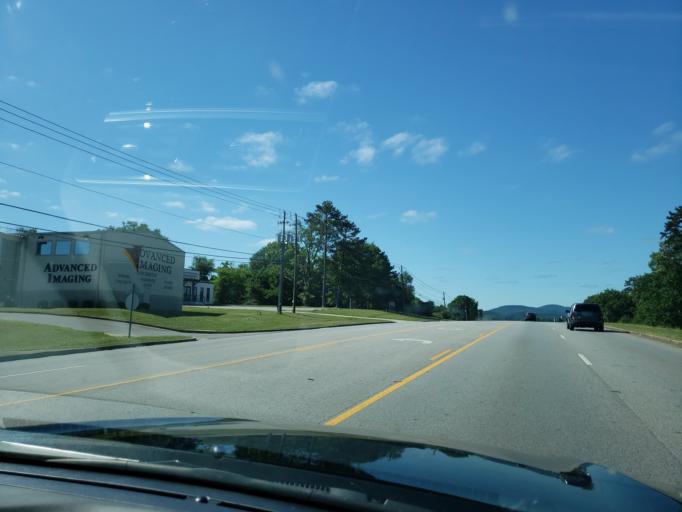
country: US
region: Alabama
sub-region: Calhoun County
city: Oxford
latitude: 33.6223
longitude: -85.7862
